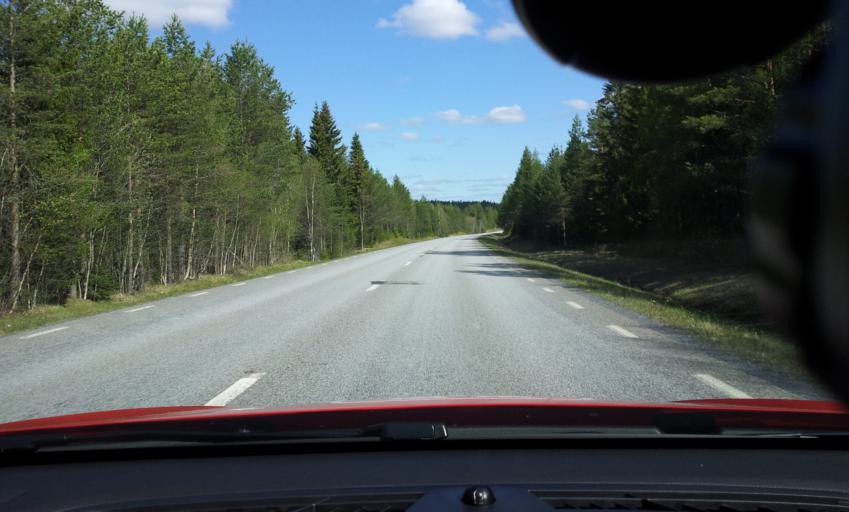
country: SE
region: Jaemtland
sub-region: Krokoms Kommun
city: Valla
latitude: 63.2868
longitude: 13.9284
